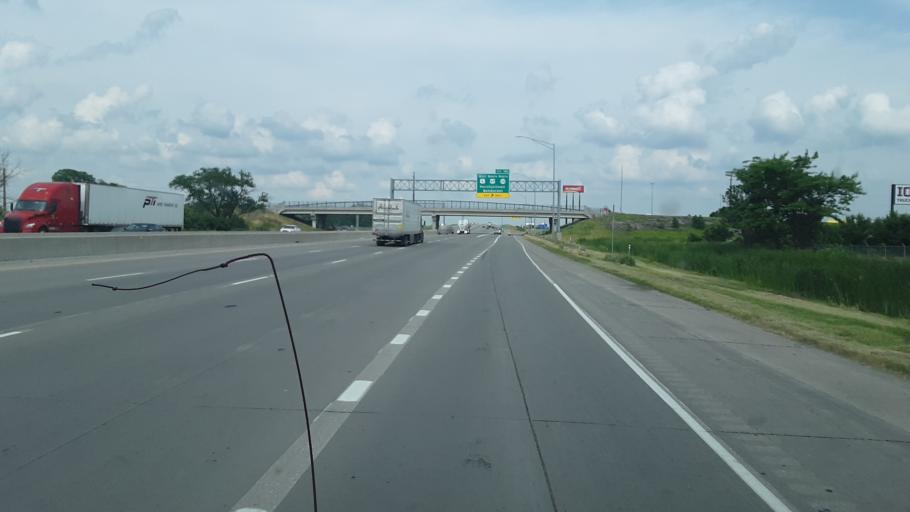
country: US
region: Iowa
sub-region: Polk County
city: Altoona
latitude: 41.6618
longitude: -93.5060
